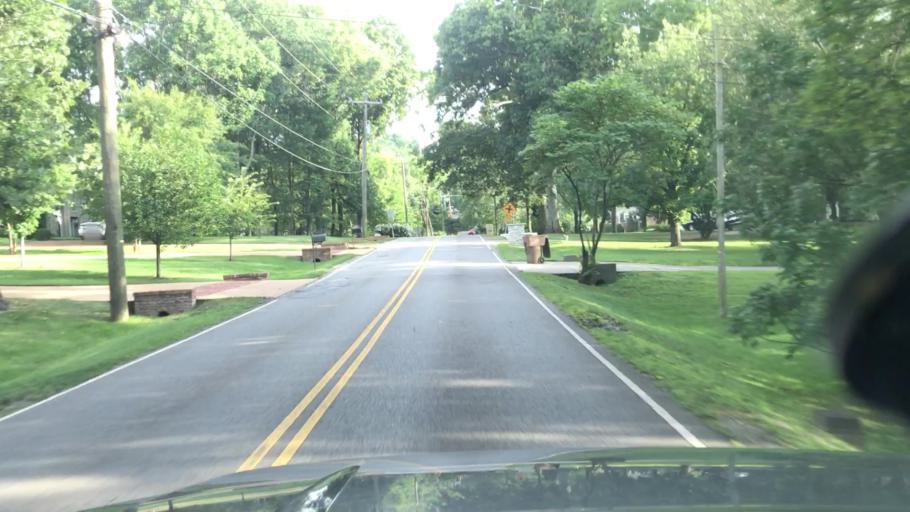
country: US
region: Tennessee
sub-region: Davidson County
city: Belle Meade
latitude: 36.0960
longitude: -86.8392
